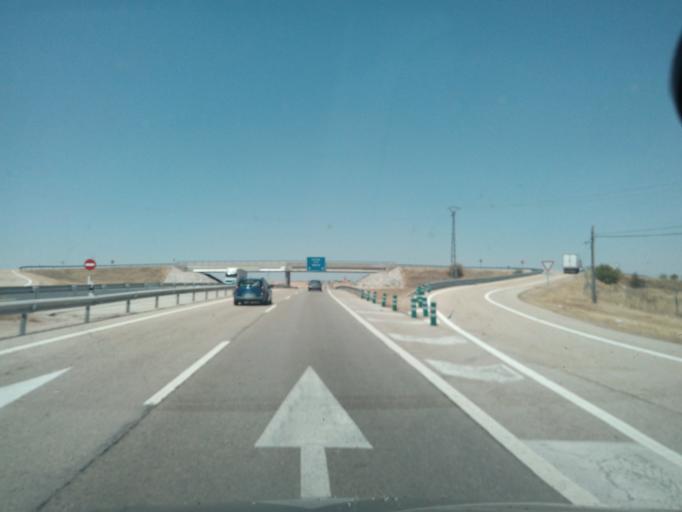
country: ES
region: Castille-La Mancha
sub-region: Province of Toledo
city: Tembleque
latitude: 39.7394
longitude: -3.4887
